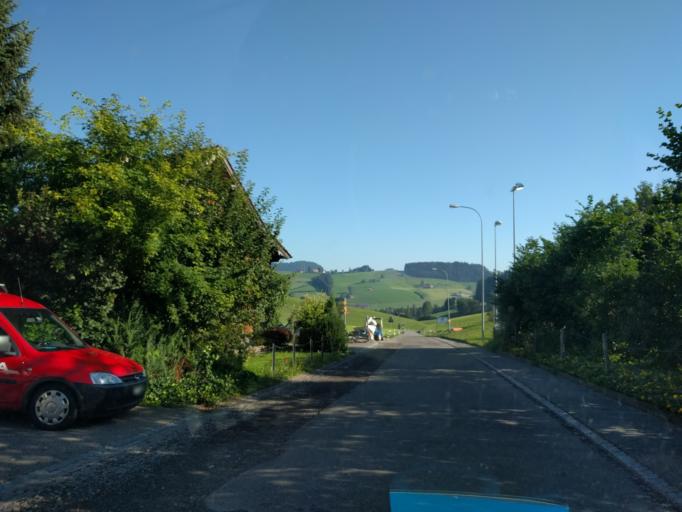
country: CH
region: Saint Gallen
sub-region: Wahlkreis Toggenburg
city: Sankt Peterzell
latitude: 47.3072
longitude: 9.1955
